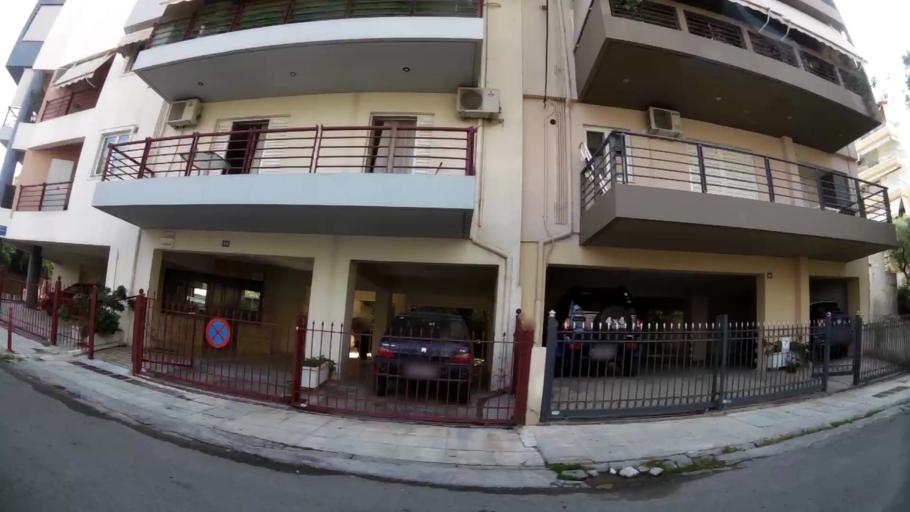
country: GR
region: Attica
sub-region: Nomarchia Athinas
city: Tavros
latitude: 37.9688
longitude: 23.7021
